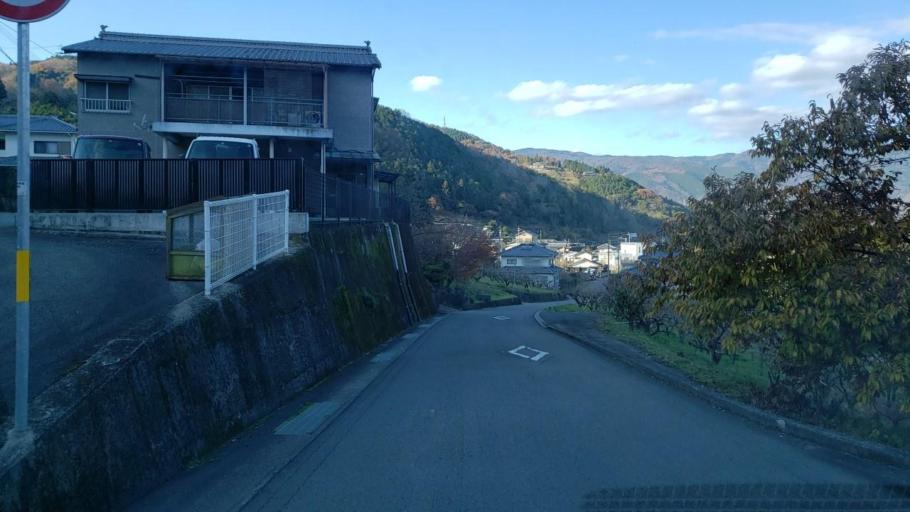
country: JP
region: Tokushima
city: Wakimachi
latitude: 34.0235
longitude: 134.0302
